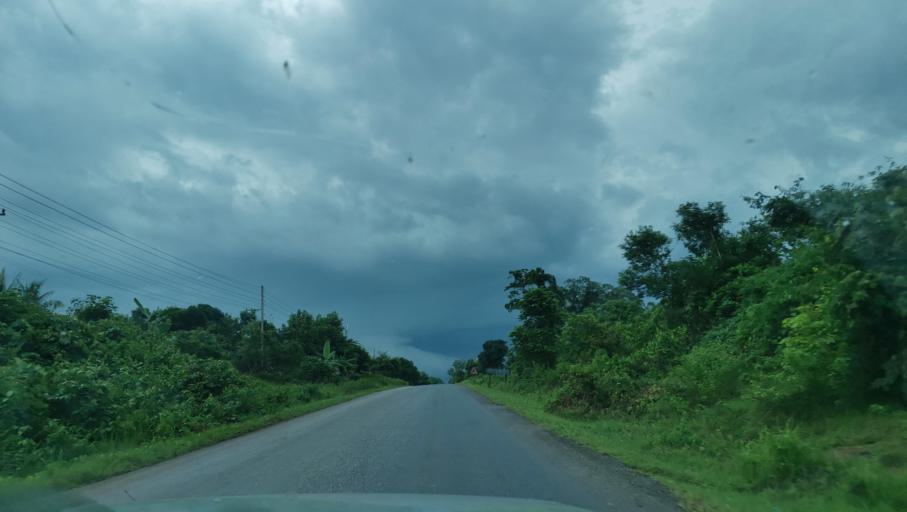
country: TH
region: Nakhon Phanom
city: Ban Phaeng
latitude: 17.8829
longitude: 104.4060
